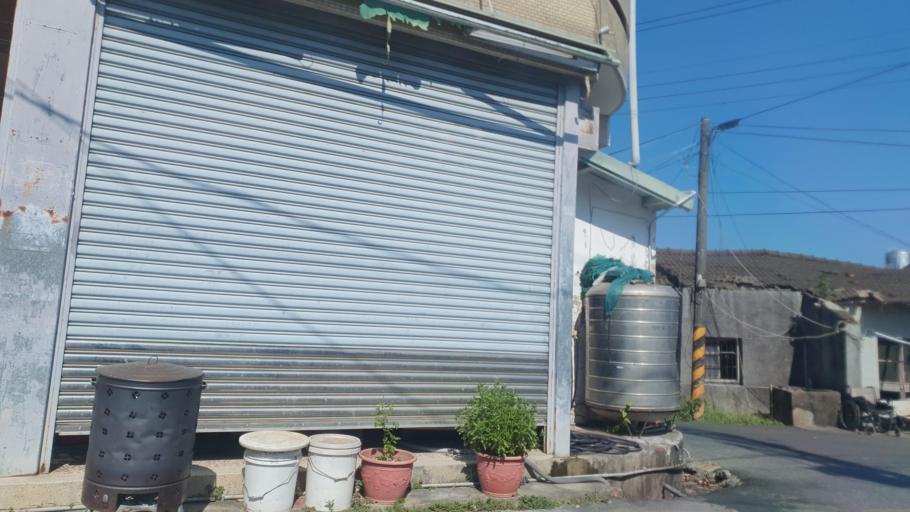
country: TW
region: Taiwan
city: Yujing
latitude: 23.0438
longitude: 120.3650
